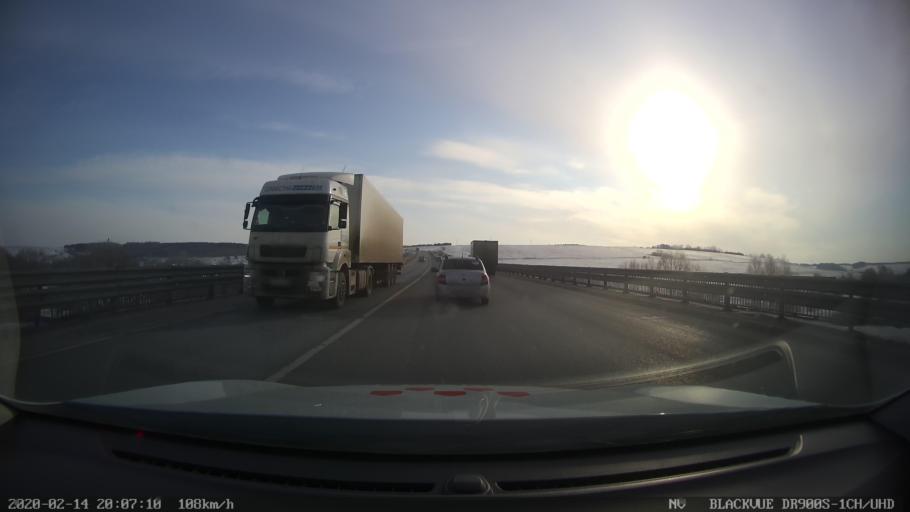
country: RU
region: Tatarstan
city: Verkhniy Uslon
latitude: 55.7219
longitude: 48.8352
